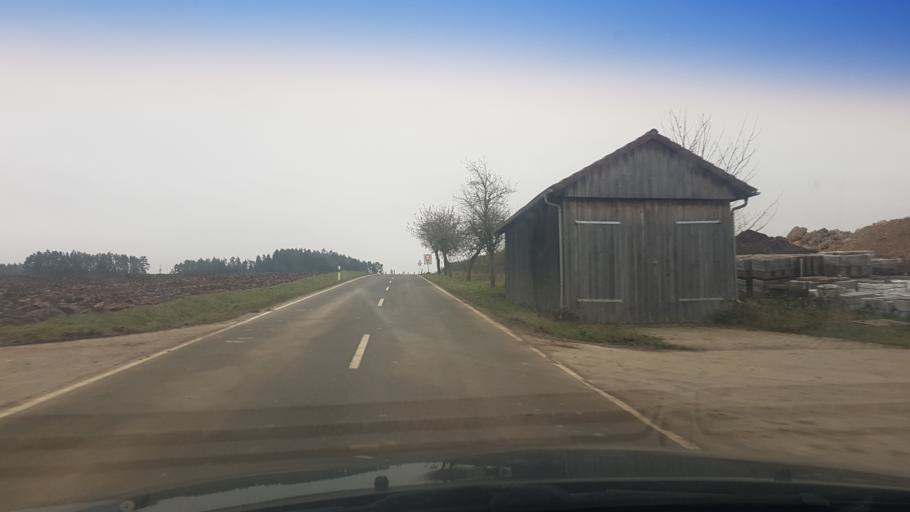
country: DE
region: Bavaria
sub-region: Upper Franconia
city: Wonsees
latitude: 50.0286
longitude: 11.2674
